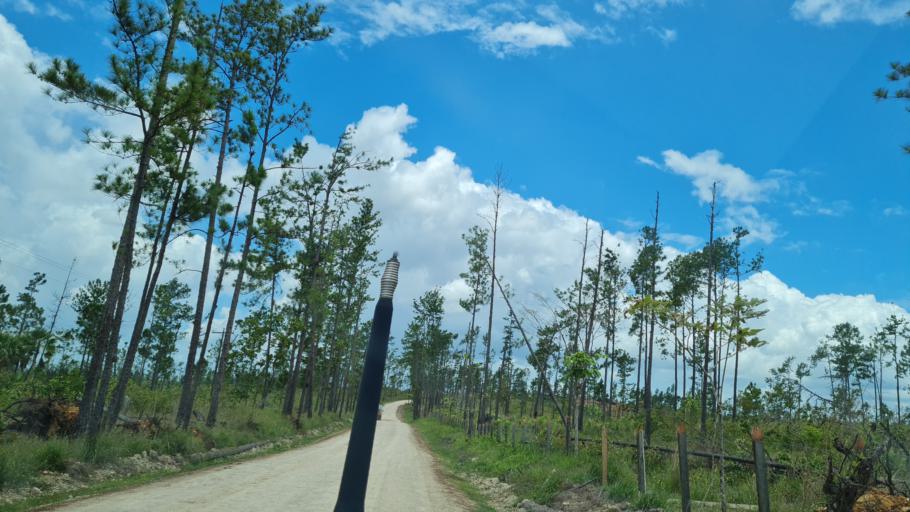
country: NI
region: Atlantico Sur
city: La Cruz de Rio Grande
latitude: 13.5698
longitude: -84.3190
